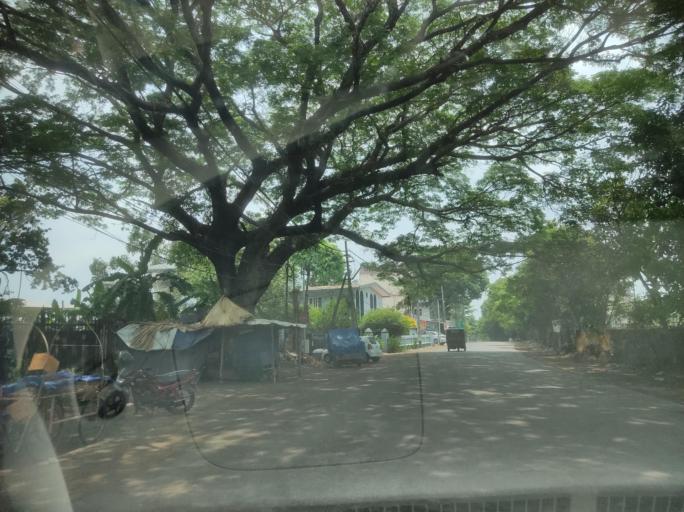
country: IN
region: Kerala
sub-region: Kottayam
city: Kottayam
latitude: 9.5916
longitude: 76.5335
